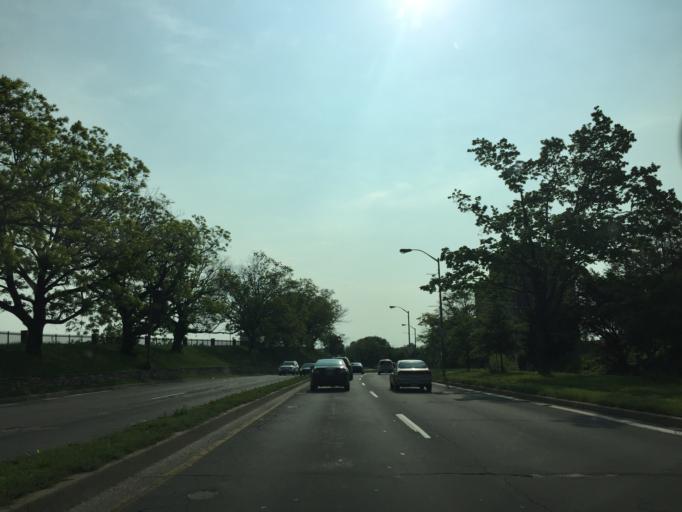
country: US
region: Maryland
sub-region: City of Baltimore
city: Baltimore
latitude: 39.3170
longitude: -76.6349
